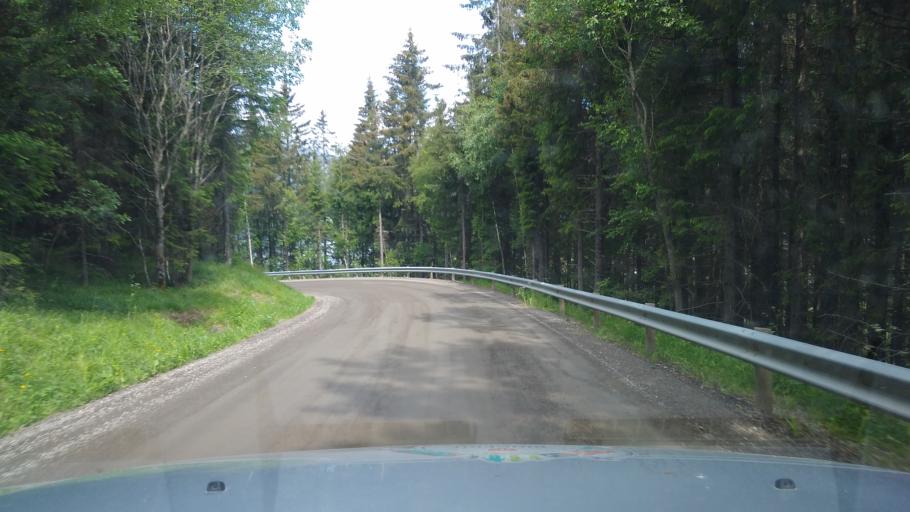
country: NO
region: Oppland
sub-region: Ringebu
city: Ringebu
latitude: 61.5198
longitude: 10.1304
